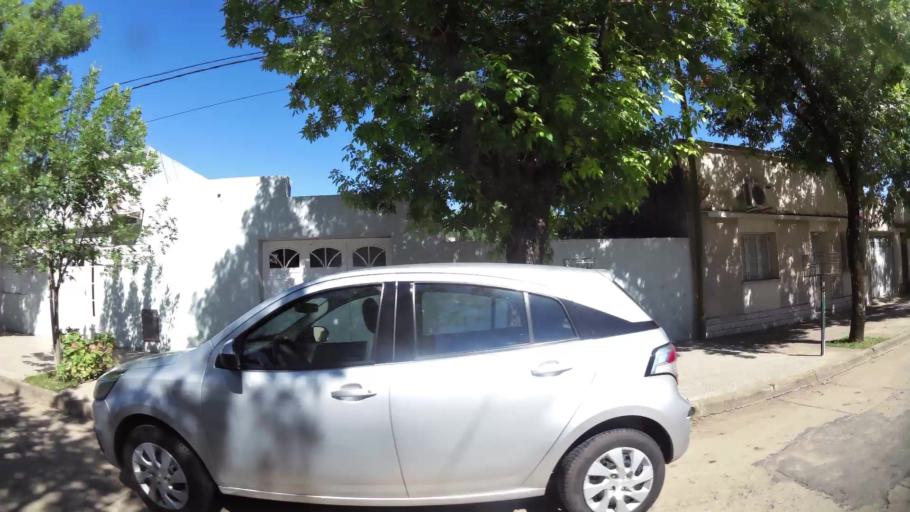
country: AR
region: Santa Fe
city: Esperanza
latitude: -31.4548
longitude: -60.9352
